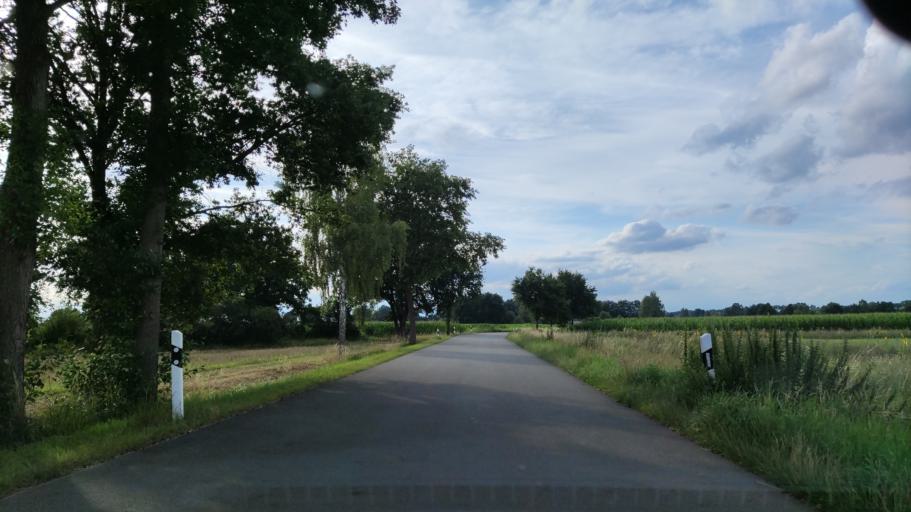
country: DE
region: Lower Saxony
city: Dannenberg
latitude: 53.0879
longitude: 11.1010
